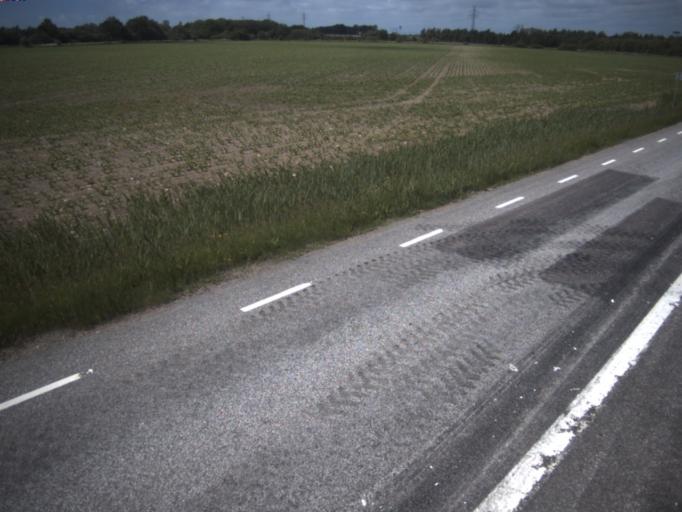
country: SE
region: Skane
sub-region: Helsingborg
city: Odakra
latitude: 56.0808
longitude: 12.7649
